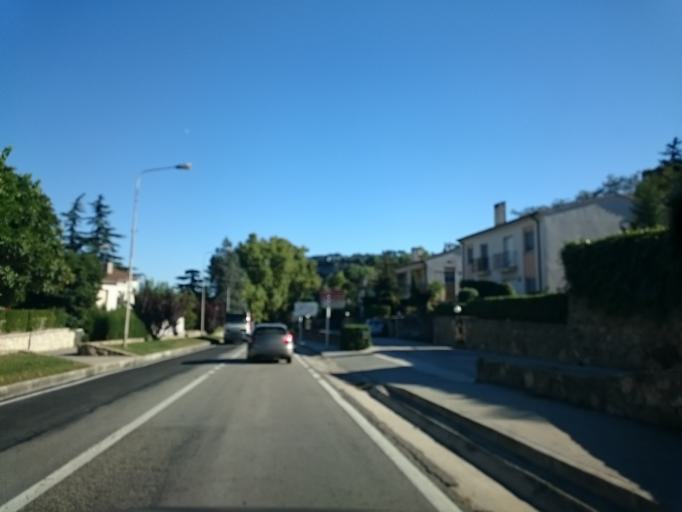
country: ES
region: Catalonia
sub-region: Provincia de Barcelona
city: Capellades
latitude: 41.5270
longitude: 1.6878
